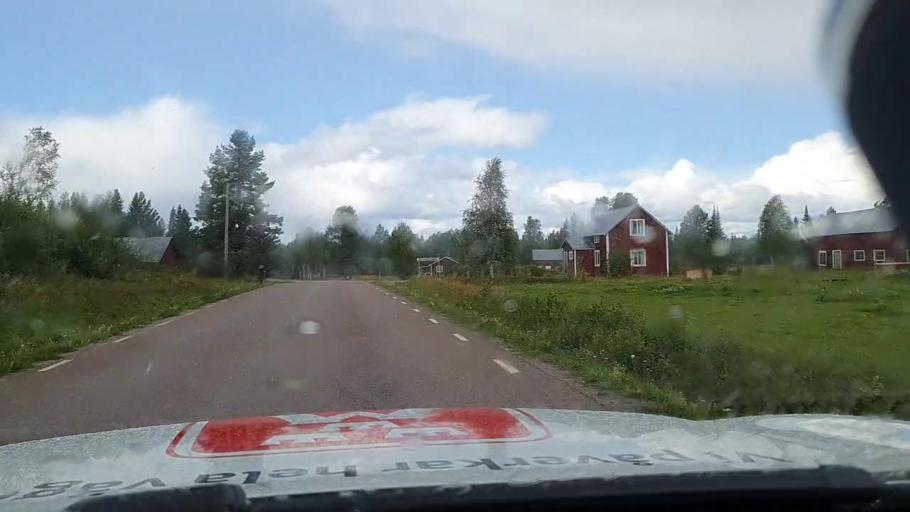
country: SE
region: Jaemtland
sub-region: Stroemsunds Kommun
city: Stroemsund
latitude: 63.8768
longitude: 15.3583
